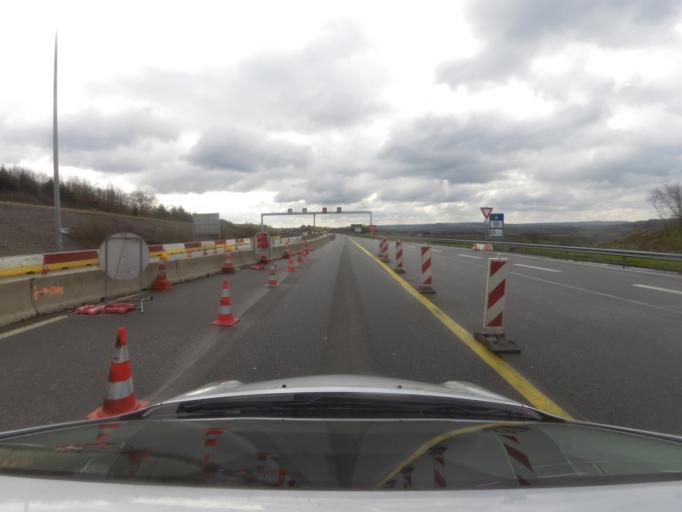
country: FR
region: Nord-Pas-de-Calais
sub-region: Departement du Pas-de-Calais
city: Saint-Etienne-au-Mont
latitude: 50.6868
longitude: 1.6439
